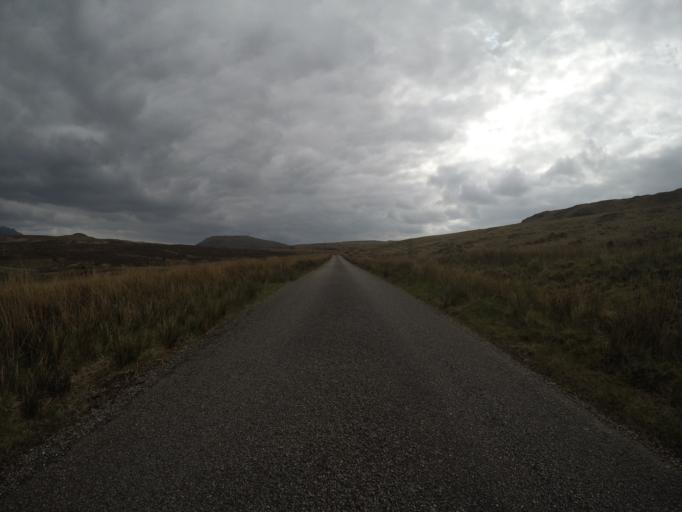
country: GB
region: Scotland
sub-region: Highland
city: Isle of Skye
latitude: 57.2947
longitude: -6.3627
